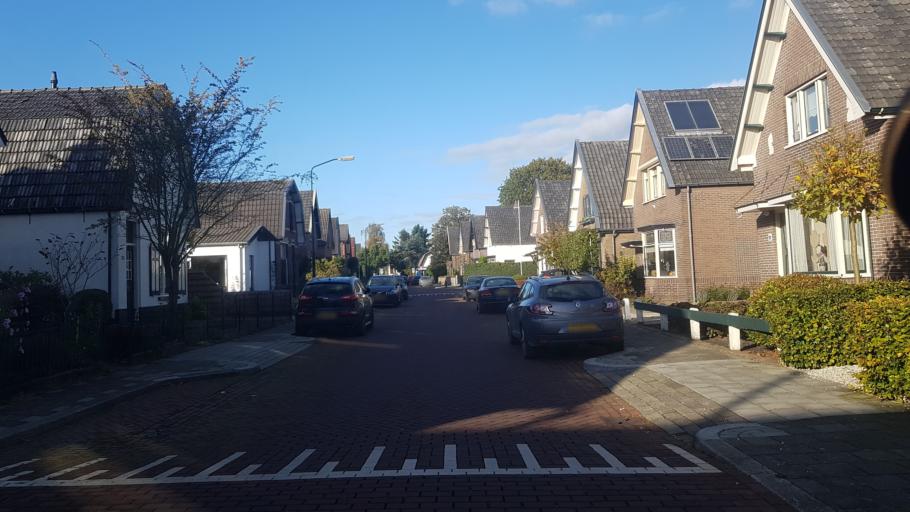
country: NL
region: Gelderland
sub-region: Gemeente Apeldoorn
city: Apeldoorn
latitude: 52.2080
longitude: 5.9452
